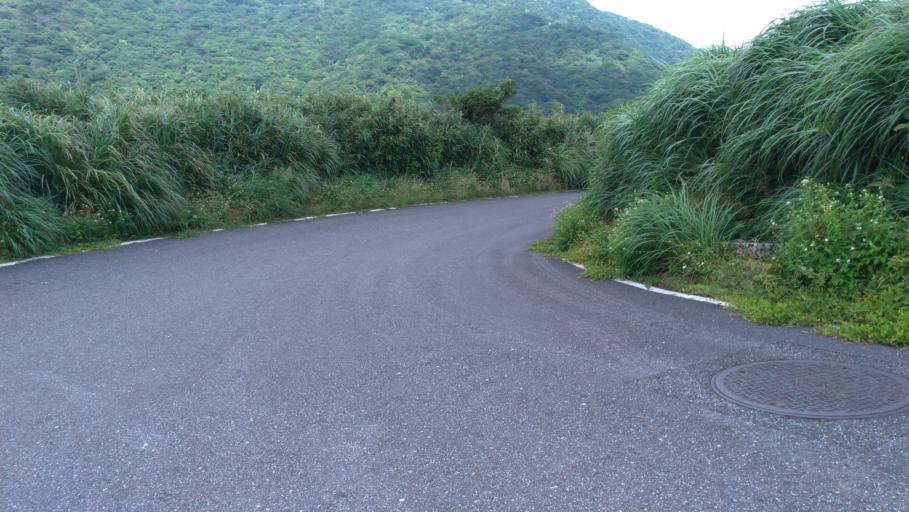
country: TW
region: Taipei
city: Taipei
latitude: 25.1838
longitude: 121.5262
